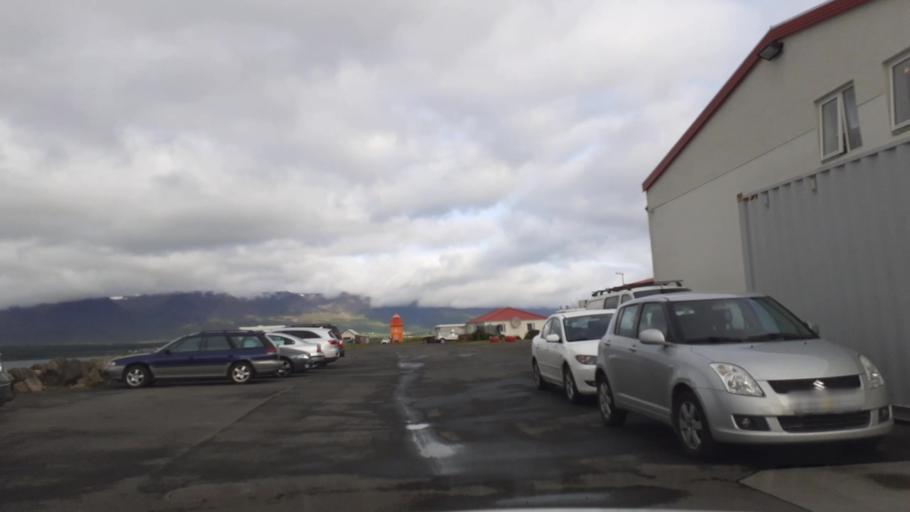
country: IS
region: Northeast
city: Akureyri
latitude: 65.7430
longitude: -18.0879
